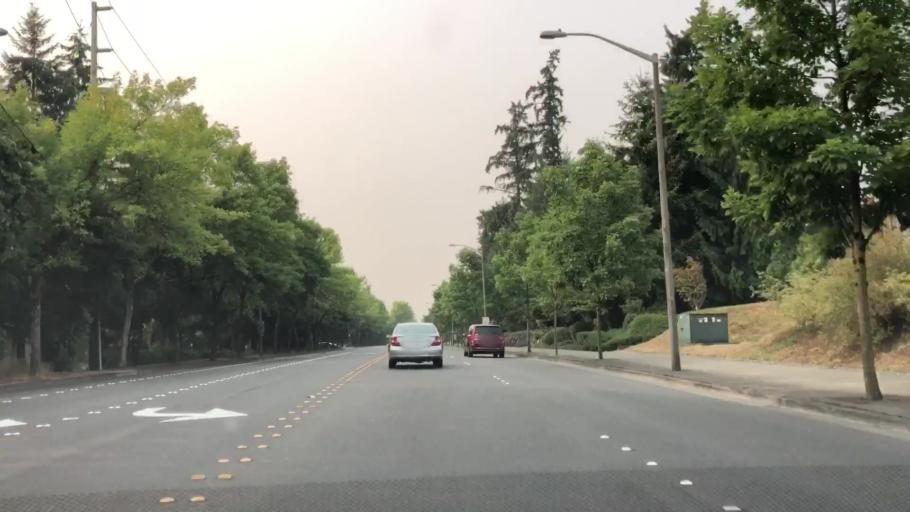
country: US
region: Washington
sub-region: King County
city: Redmond
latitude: 47.6537
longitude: -122.1325
